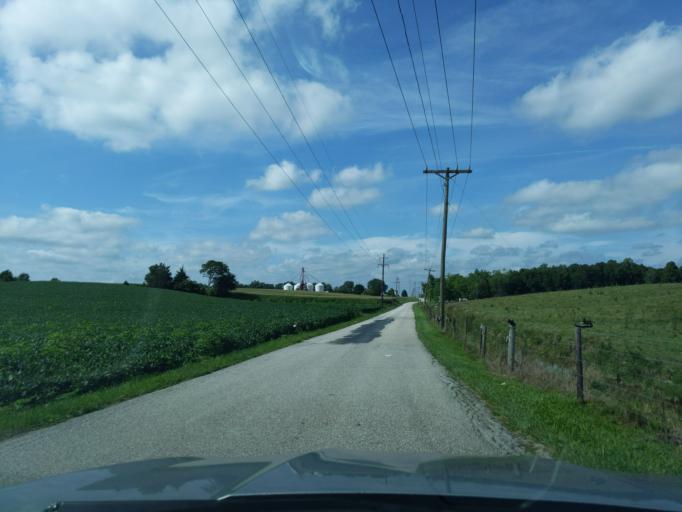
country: US
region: Indiana
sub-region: Ripley County
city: Batesville
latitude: 39.2524
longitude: -85.3475
